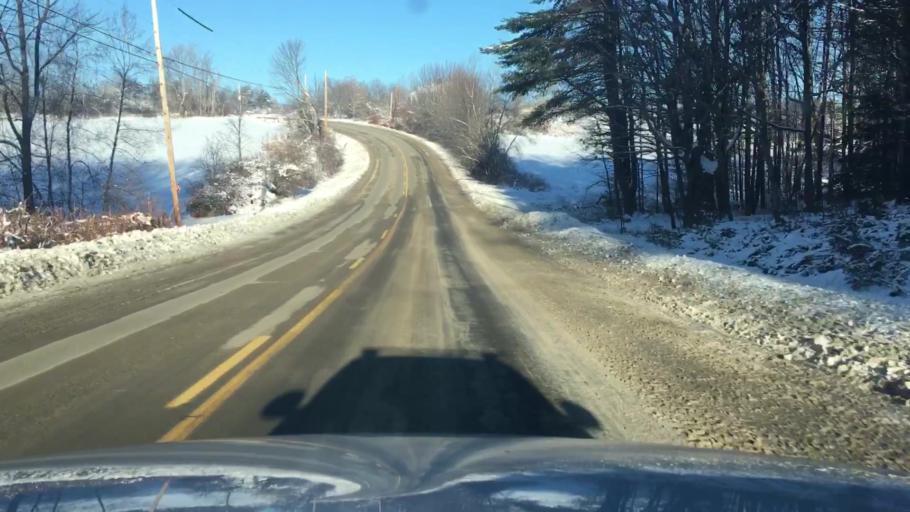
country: US
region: Maine
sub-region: Kennebec County
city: Readfield
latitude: 44.4287
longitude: -69.9367
